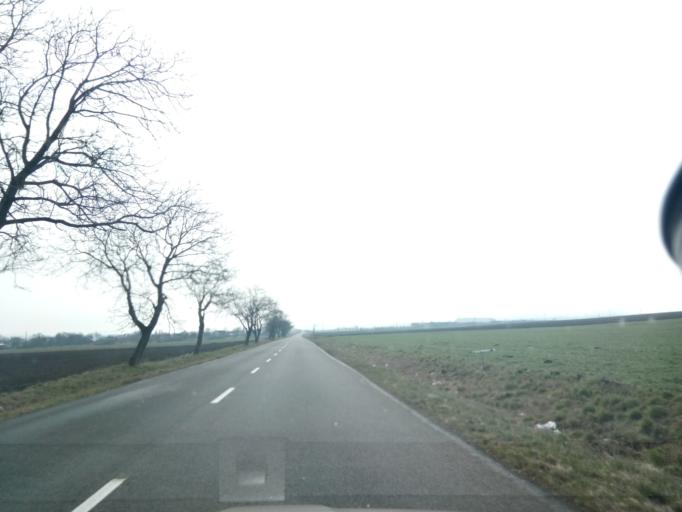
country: SK
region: Kosicky
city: Trebisov
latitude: 48.5734
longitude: 21.6443
